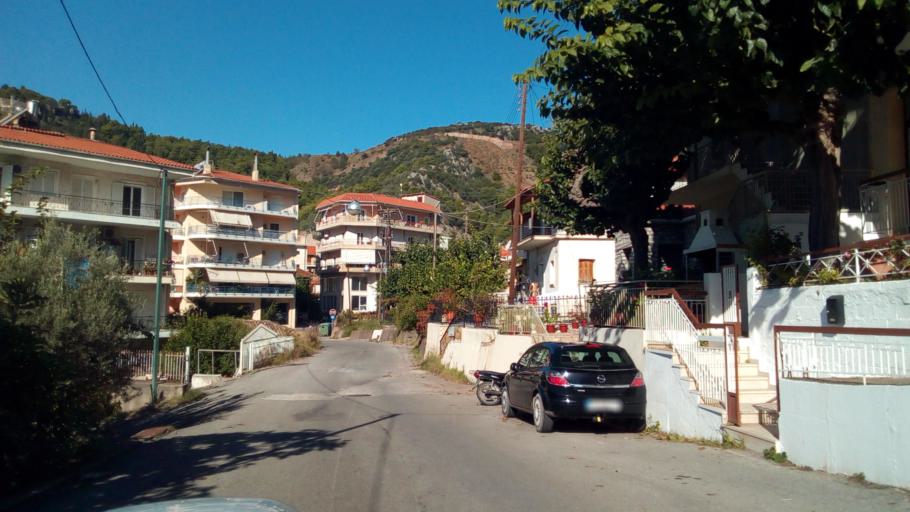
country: GR
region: West Greece
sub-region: Nomos Aitolias kai Akarnanias
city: Nafpaktos
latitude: 38.3966
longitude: 21.8335
